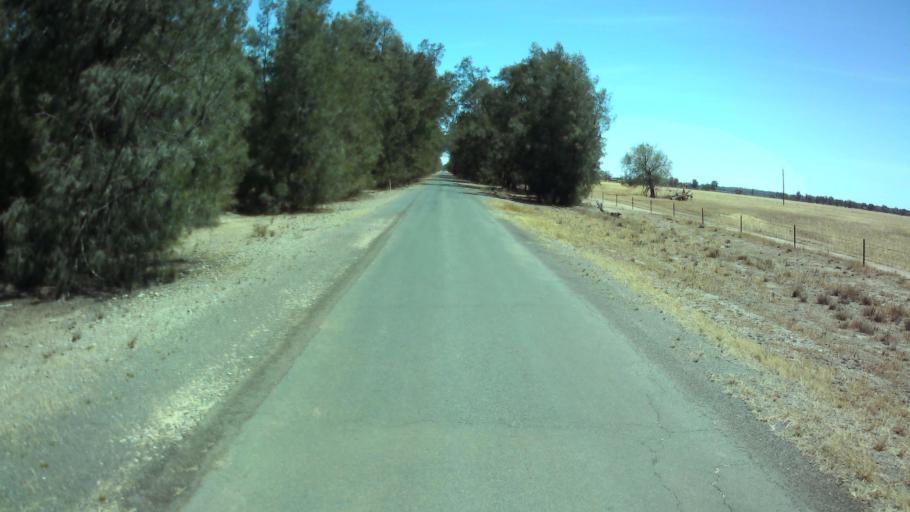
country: AU
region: New South Wales
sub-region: Weddin
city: Grenfell
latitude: -33.8821
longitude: 147.6898
